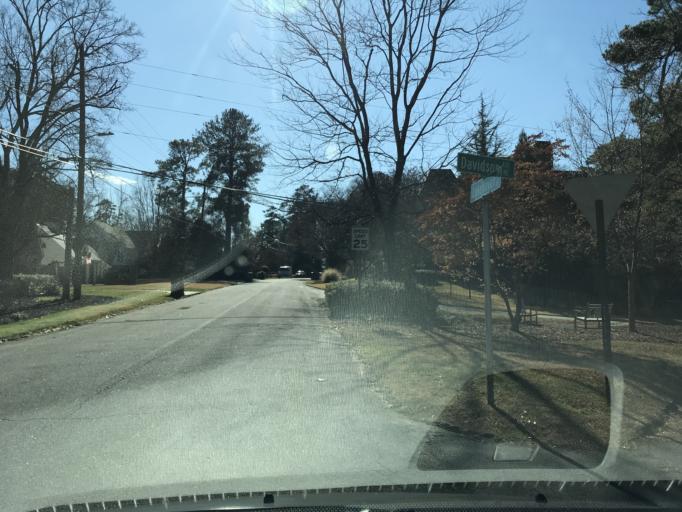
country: US
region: Georgia
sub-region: DeKalb County
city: North Atlanta
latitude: 33.8738
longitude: -84.3505
